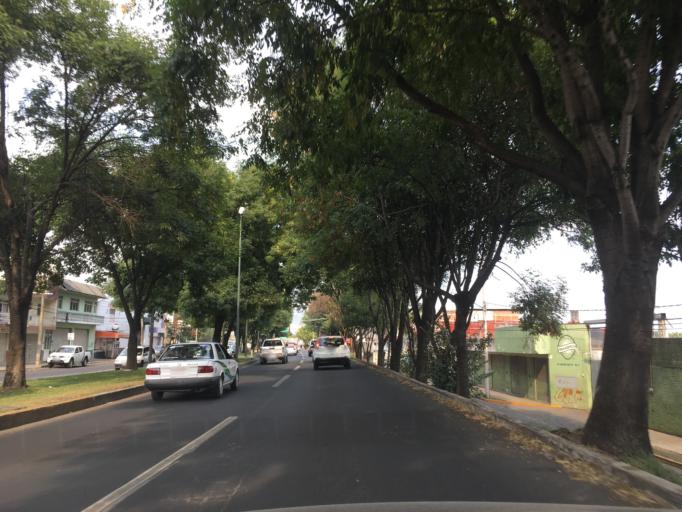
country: MX
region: Michoacan
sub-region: Uruapan
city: Uruapan
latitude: 19.4256
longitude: -102.0445
